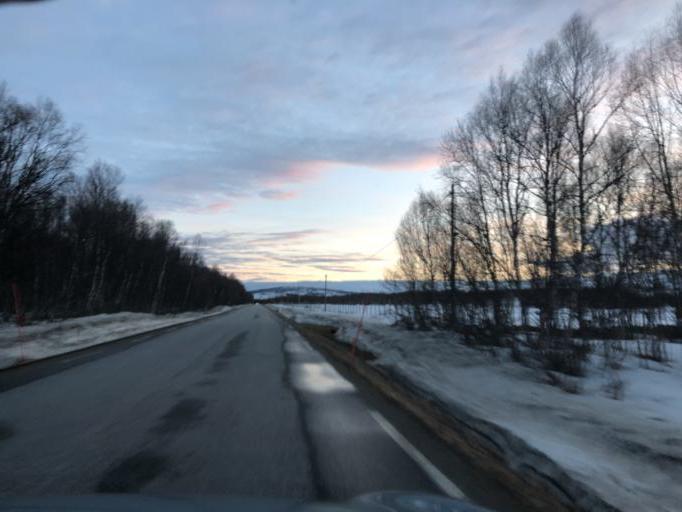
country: NO
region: Sor-Trondelag
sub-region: Tydal
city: Aas
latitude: 62.6778
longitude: 11.8462
